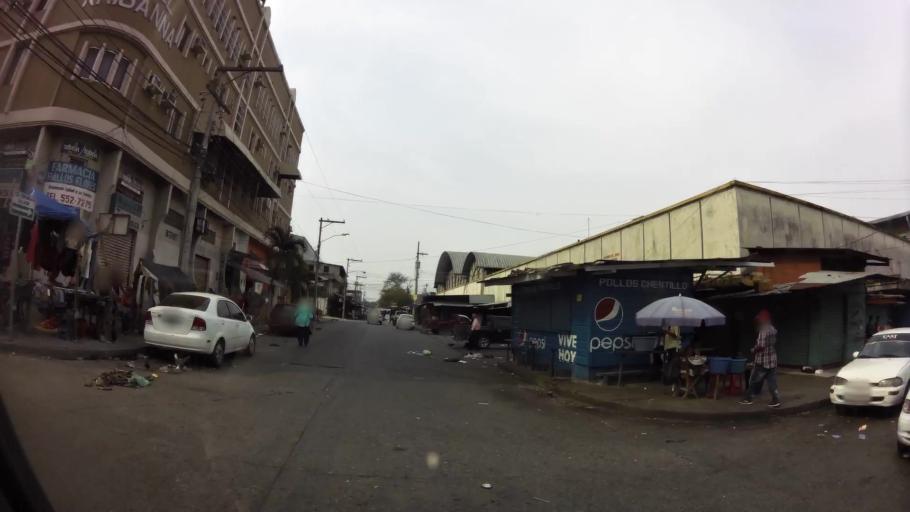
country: HN
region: Cortes
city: San Pedro Sula
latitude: 15.4999
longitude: -88.0206
